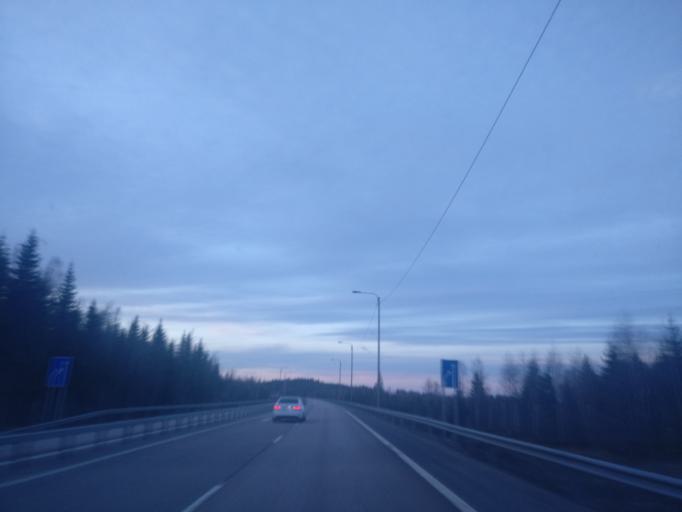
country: FI
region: Central Finland
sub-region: Jyvaeskylae
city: Saeynaetsalo
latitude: 62.1705
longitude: 25.9051
